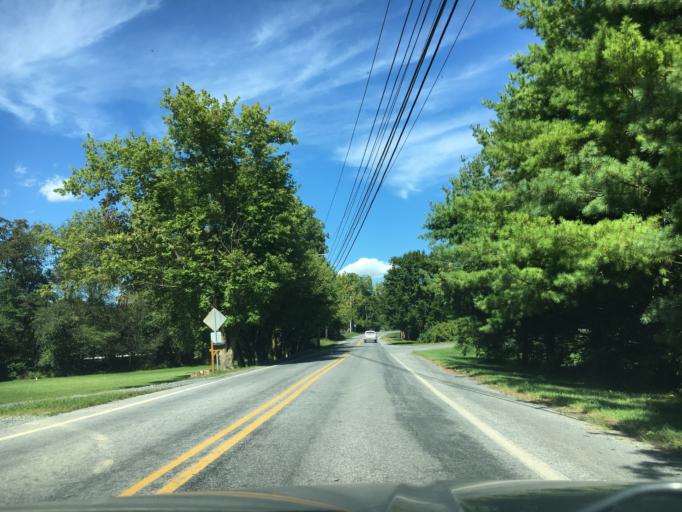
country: US
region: Pennsylvania
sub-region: Berks County
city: Topton
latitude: 40.5199
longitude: -75.6895
